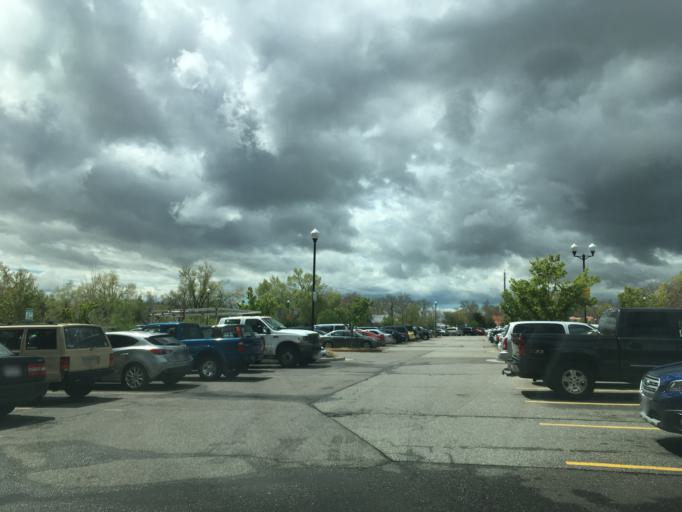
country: US
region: Utah
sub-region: Davis County
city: Layton
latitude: 41.0594
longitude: -111.9667
